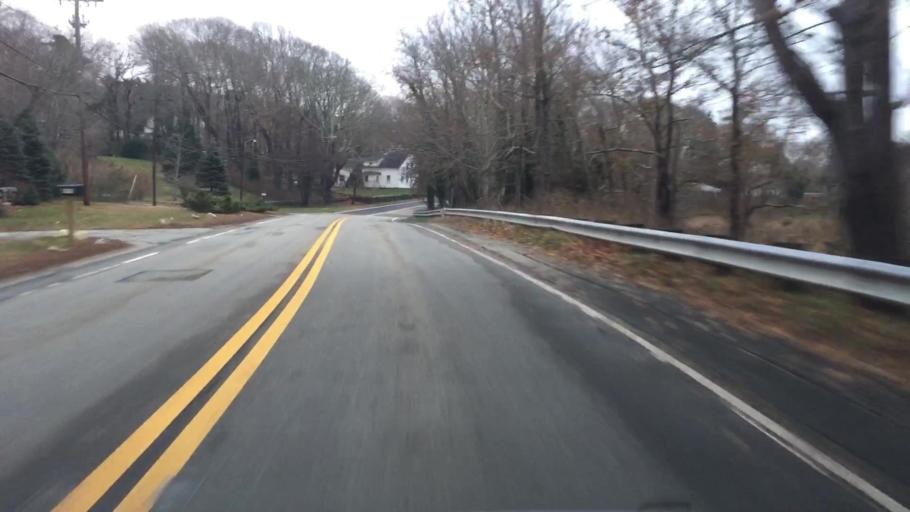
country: US
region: Massachusetts
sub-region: Barnstable County
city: West Falmouth
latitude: 41.5970
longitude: -70.6365
